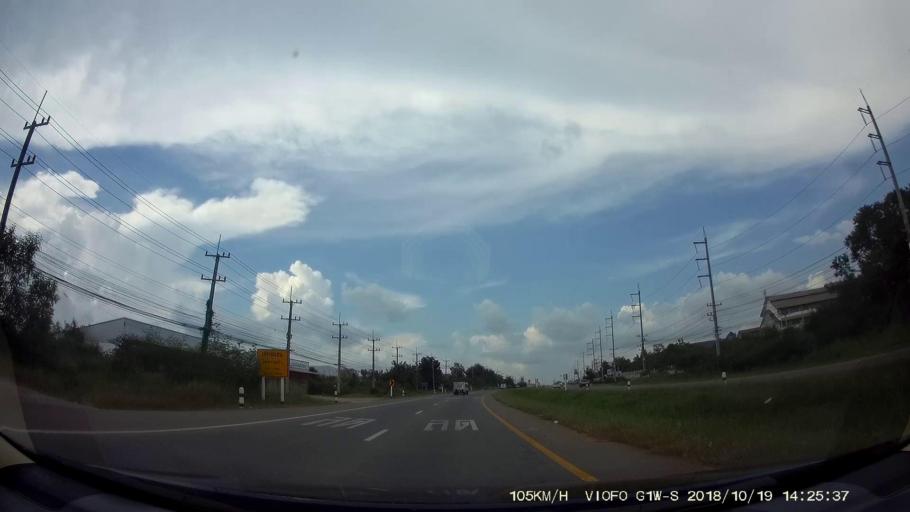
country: TH
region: Chaiyaphum
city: Kaeng Khro
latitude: 16.0961
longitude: 102.2636
